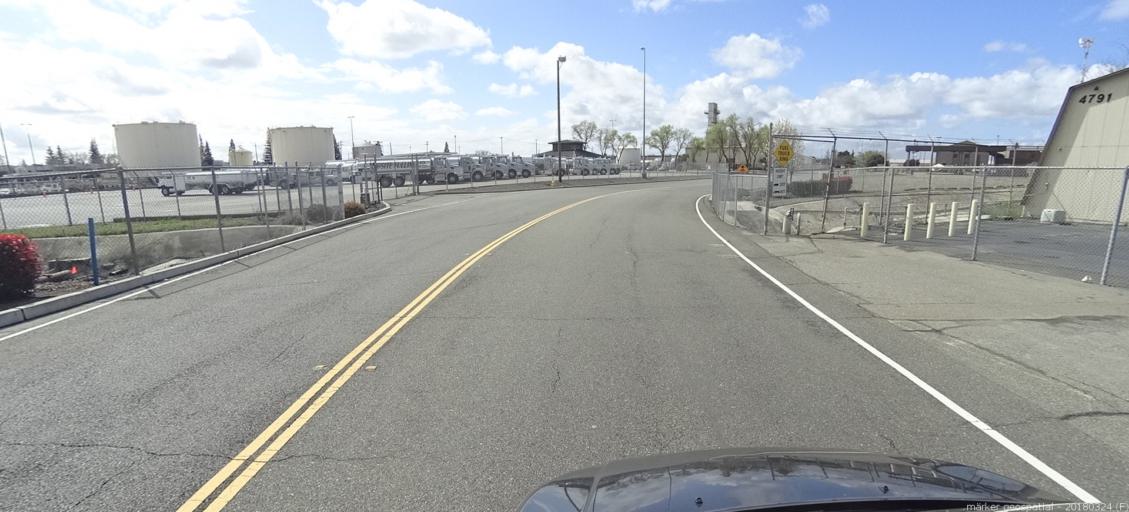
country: US
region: California
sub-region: Sacramento County
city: North Highlands
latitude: 38.6550
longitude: -121.3920
